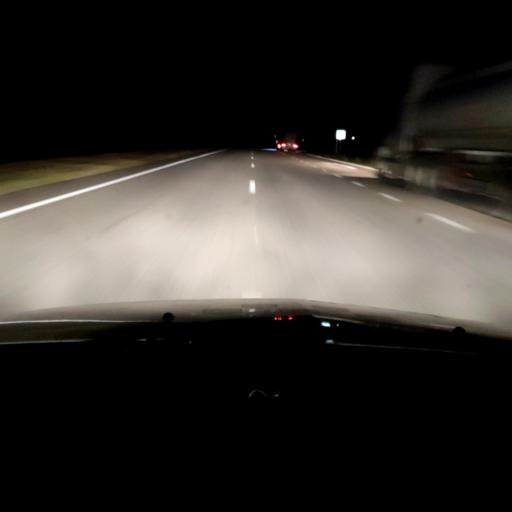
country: RU
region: Belgorod
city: Skorodnoye
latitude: 51.0578
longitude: 37.2031
